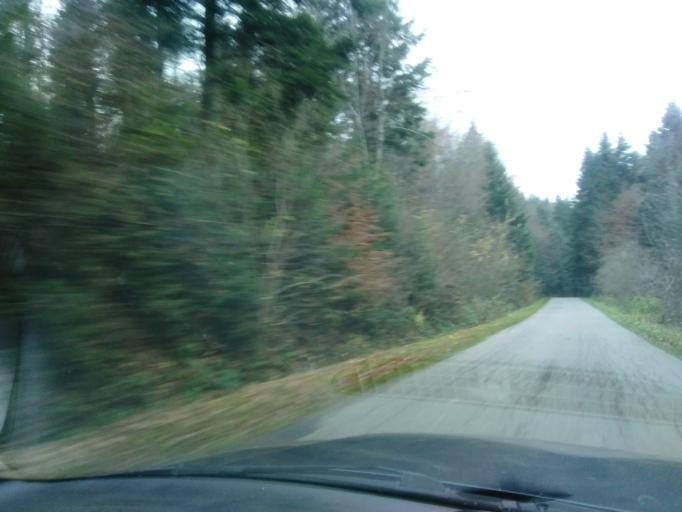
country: PL
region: Subcarpathian Voivodeship
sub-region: Powiat strzyzowski
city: Wysoka Strzyzowska
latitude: 49.8287
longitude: 21.7766
